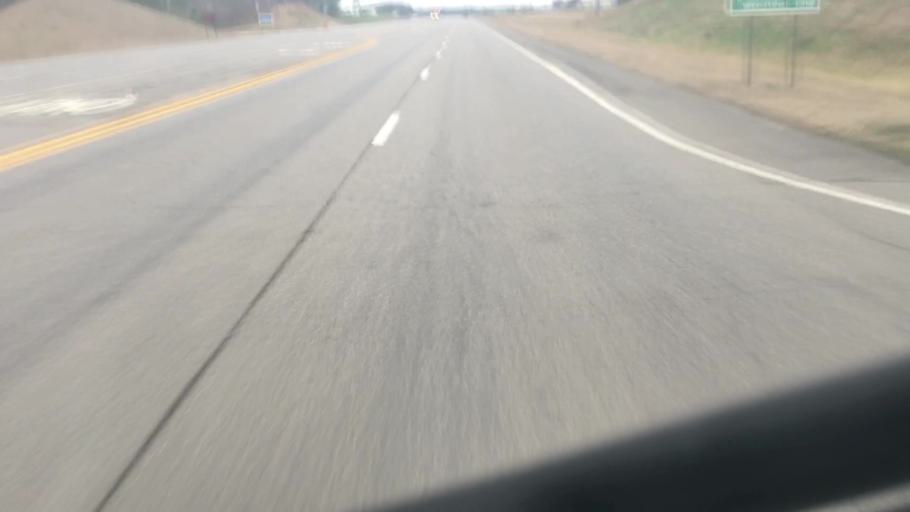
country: US
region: Alabama
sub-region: Walker County
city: Jasper
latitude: 33.8067
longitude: -87.2348
